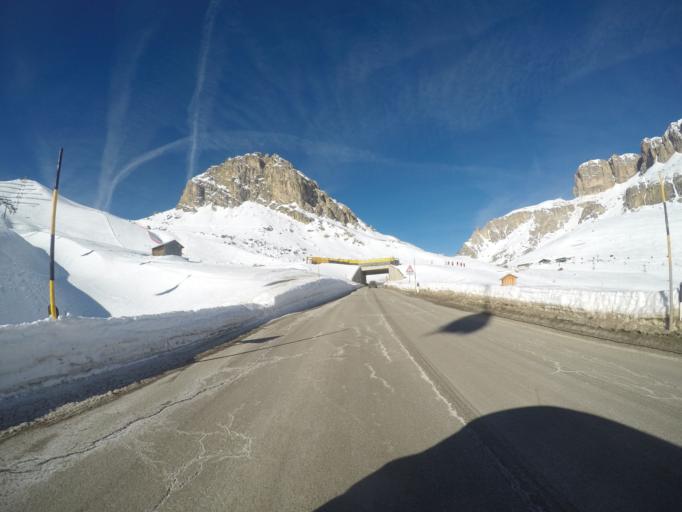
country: IT
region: Trentino-Alto Adige
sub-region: Provincia di Trento
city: Canazei
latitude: 46.4832
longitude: 11.8201
